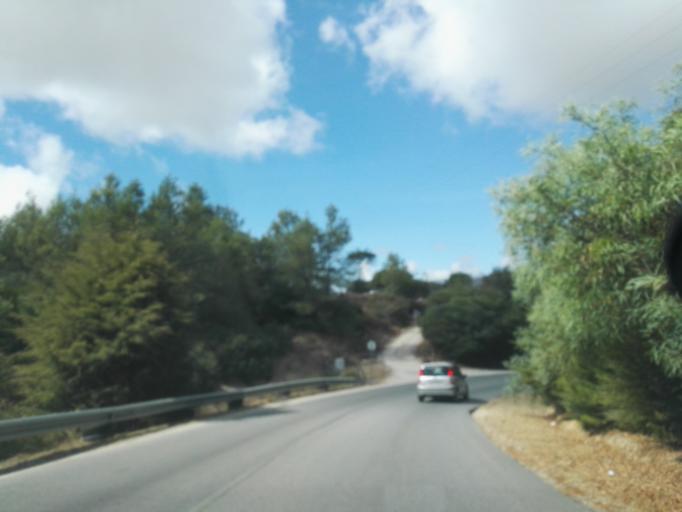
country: PT
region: Setubal
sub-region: Sesimbra
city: Sesimbra
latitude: 38.4619
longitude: -9.0960
